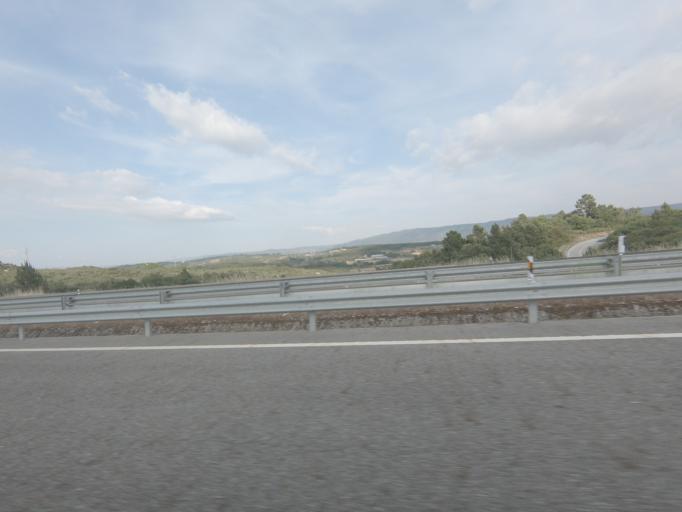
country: PT
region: Vila Real
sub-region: Chaves
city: Chaves
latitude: 41.7233
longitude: -7.5426
